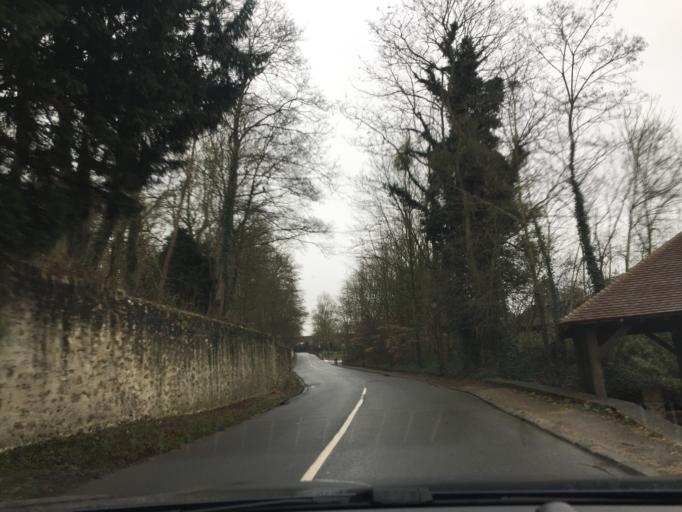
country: FR
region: Ile-de-France
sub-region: Departement de Seine-et-Marne
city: Coupvray
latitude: 48.8908
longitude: 2.7928
